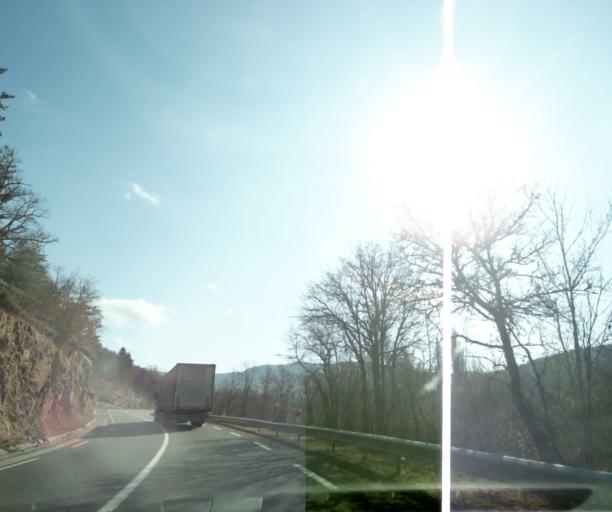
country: FR
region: Languedoc-Roussillon
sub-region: Departement de la Lozere
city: Chirac
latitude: 44.4906
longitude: 3.2673
